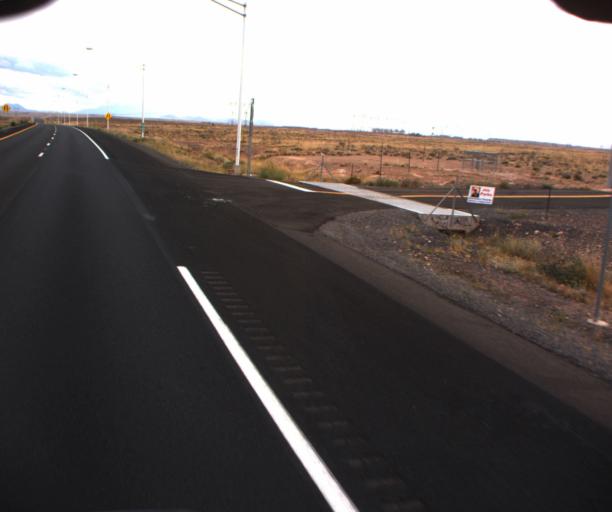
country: US
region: Arizona
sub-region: Coconino County
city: Tuba City
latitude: 35.8405
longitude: -111.4356
